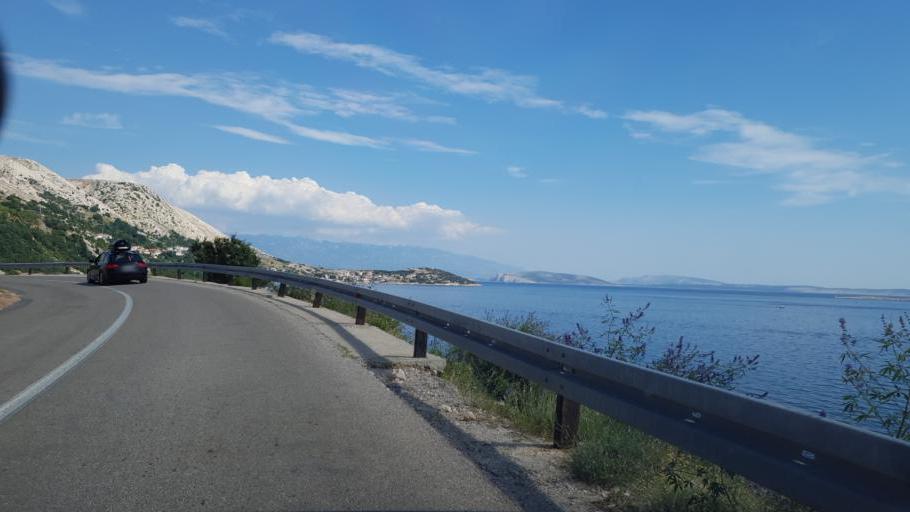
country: HR
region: Primorsko-Goranska
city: Punat
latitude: 44.9662
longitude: 14.6694
